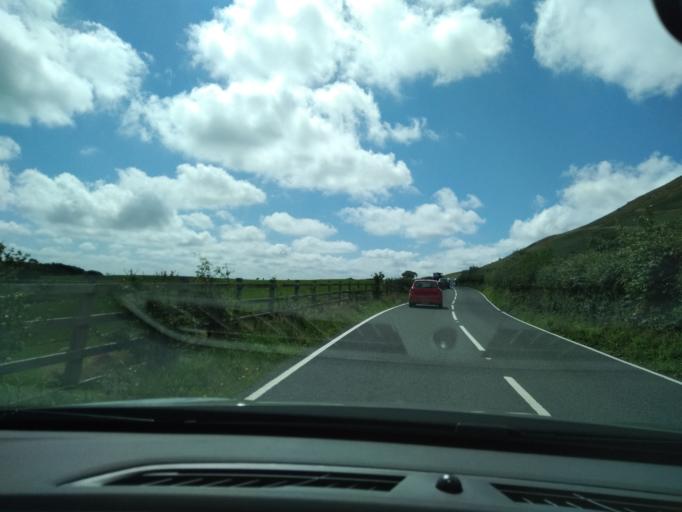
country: GB
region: England
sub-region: Cumbria
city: Millom
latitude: 54.2410
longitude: -3.3186
